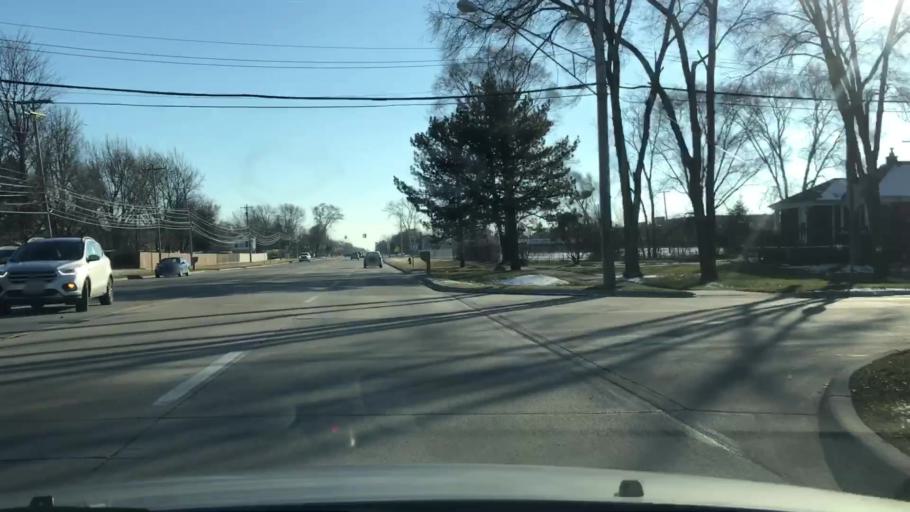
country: US
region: Michigan
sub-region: Oakland County
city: Troy
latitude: 42.5853
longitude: -83.1093
